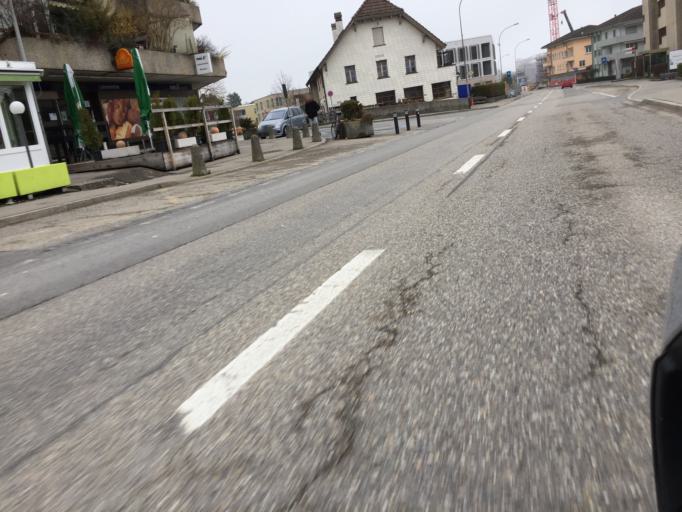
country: CH
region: Bern
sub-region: Biel/Bienne District
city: Orpund
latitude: 47.1390
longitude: 7.3073
